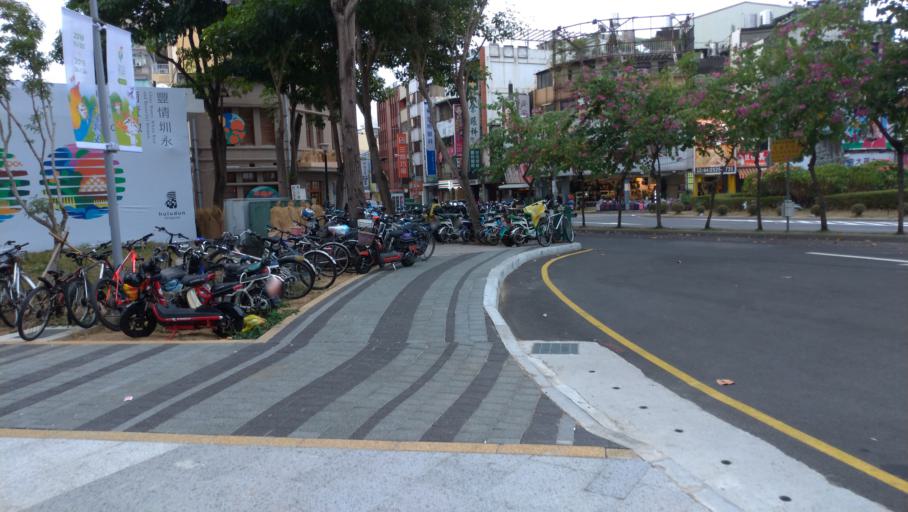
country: TW
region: Taiwan
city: Fengyuan
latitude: 24.2540
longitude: 120.7229
